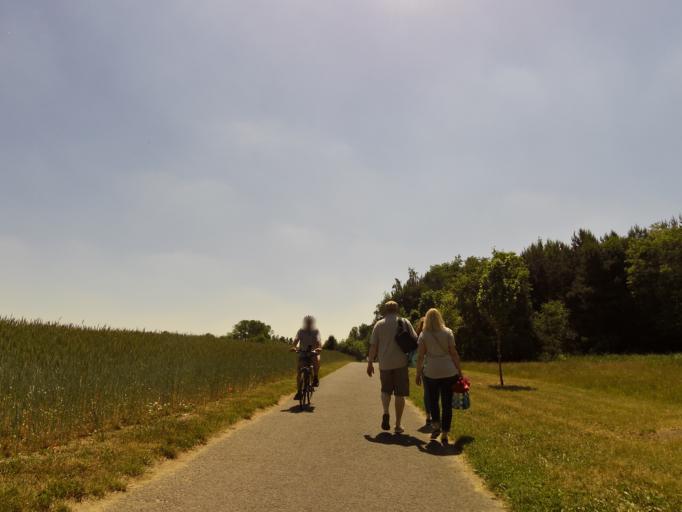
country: DE
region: Hesse
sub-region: Regierungsbezirk Darmstadt
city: Erzhausen
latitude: 49.9683
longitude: 8.6413
